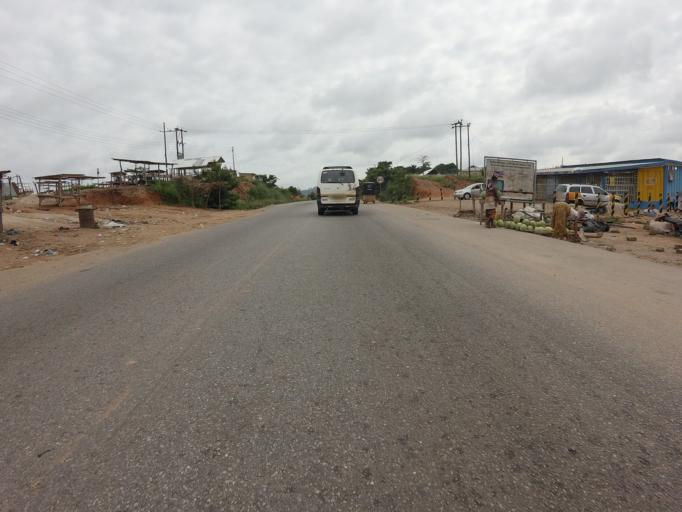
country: GH
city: Bechem
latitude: 7.1238
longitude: -1.7339
